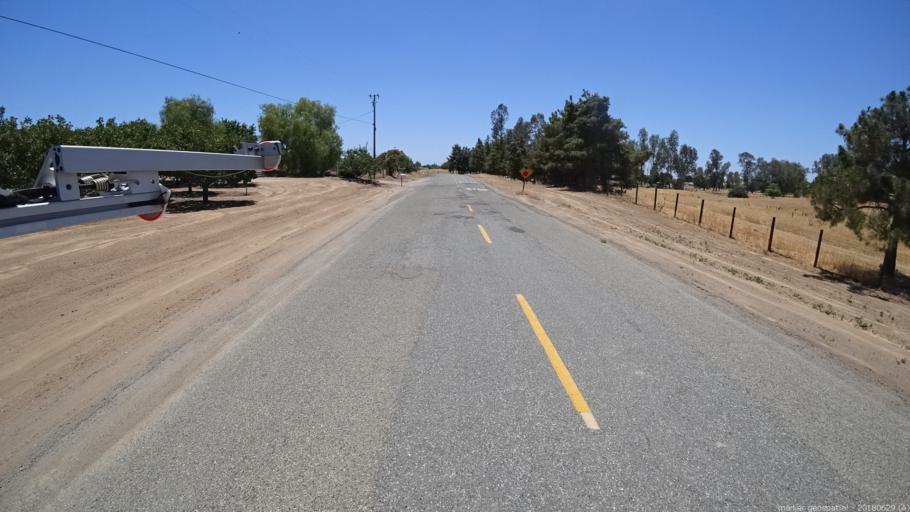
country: US
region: California
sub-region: Madera County
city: Parksdale
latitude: 37.0007
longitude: -119.9768
